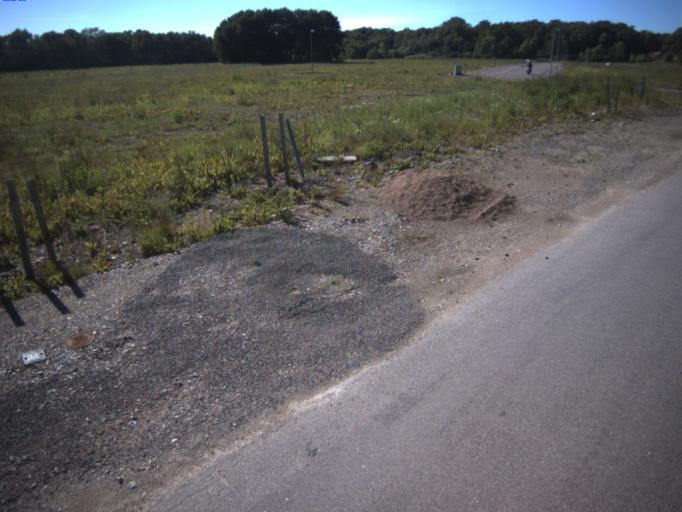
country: SE
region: Skane
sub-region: Helsingborg
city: Odakra
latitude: 56.0970
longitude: 12.7446
